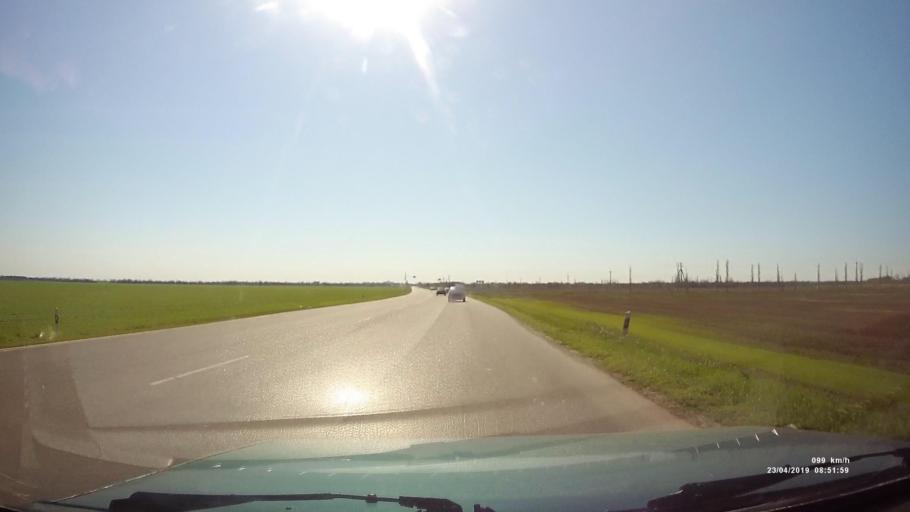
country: RU
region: Rostov
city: Sal'sk
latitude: 46.4844
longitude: 41.4515
